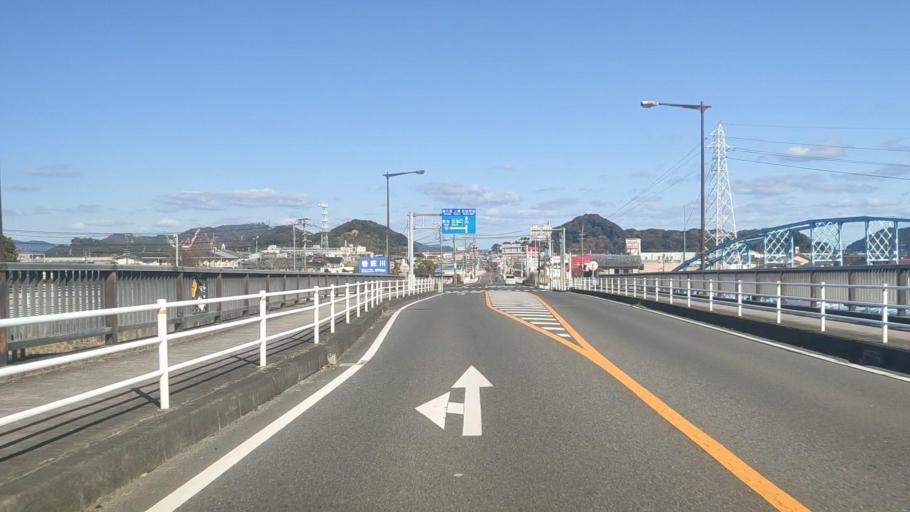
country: JP
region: Oita
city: Saiki
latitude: 32.9492
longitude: 131.9034
